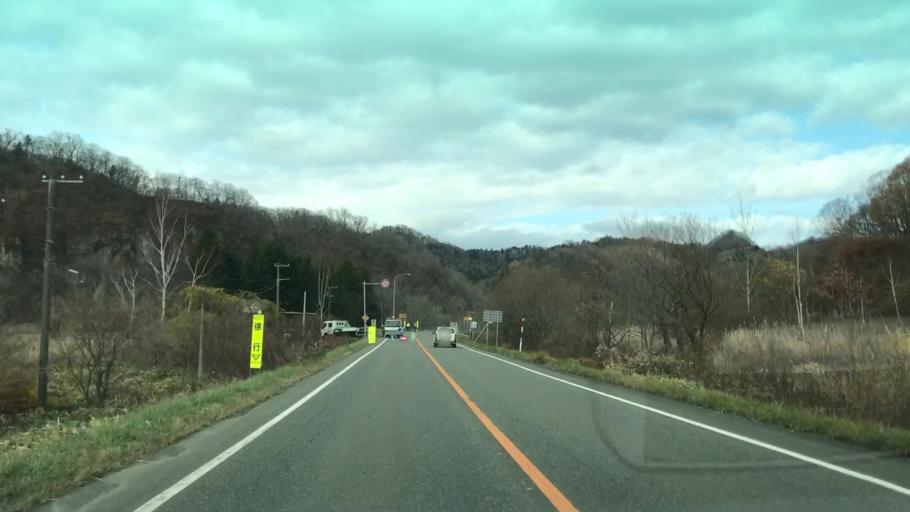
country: JP
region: Hokkaido
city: Shizunai-furukawacho
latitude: 42.7920
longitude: 142.3939
